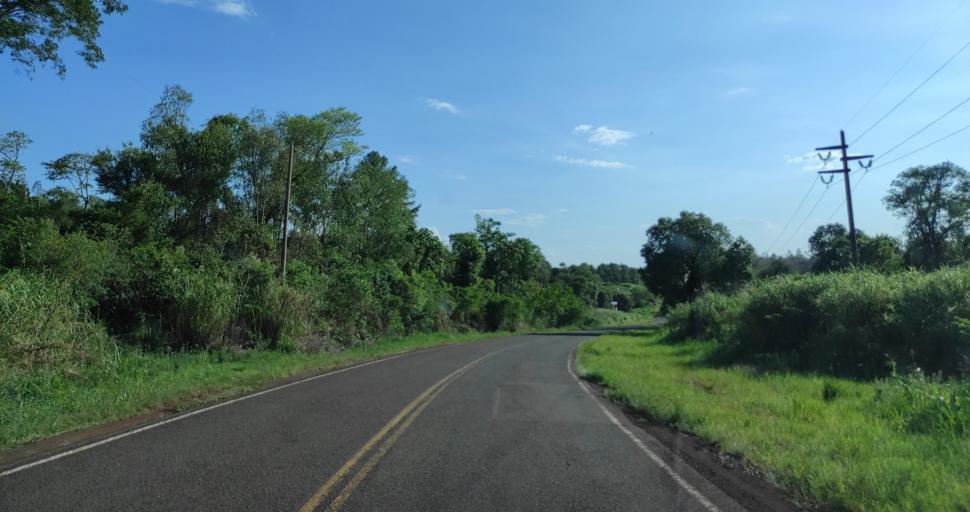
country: AR
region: Misiones
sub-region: Departamento de Eldorado
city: Eldorado
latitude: -26.3789
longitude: -54.3378
